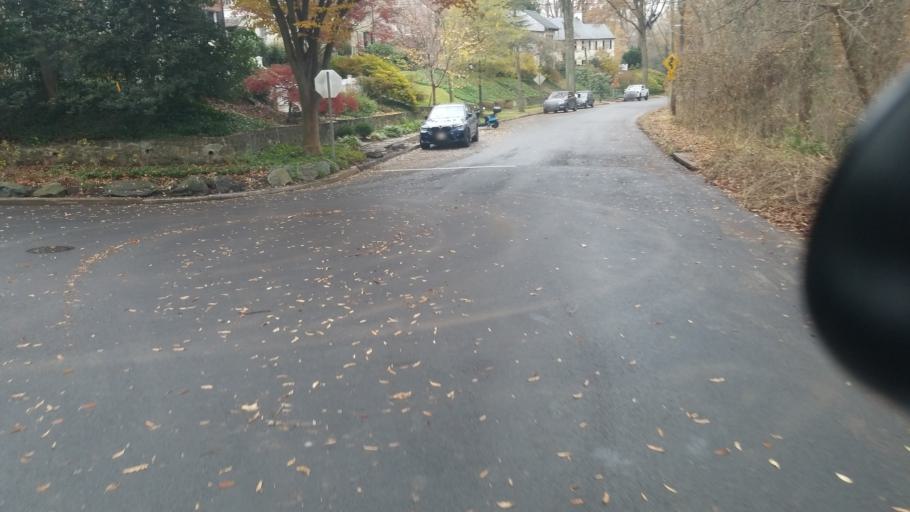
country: US
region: Maryland
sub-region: Montgomery County
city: Brookmont
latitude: 38.9277
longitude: -77.0936
